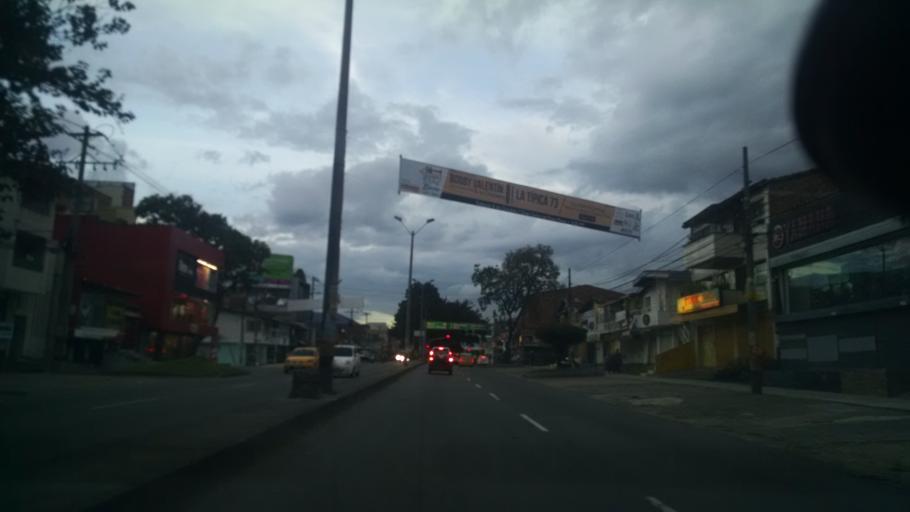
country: CO
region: Antioquia
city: Medellin
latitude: 6.2451
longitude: -75.6027
